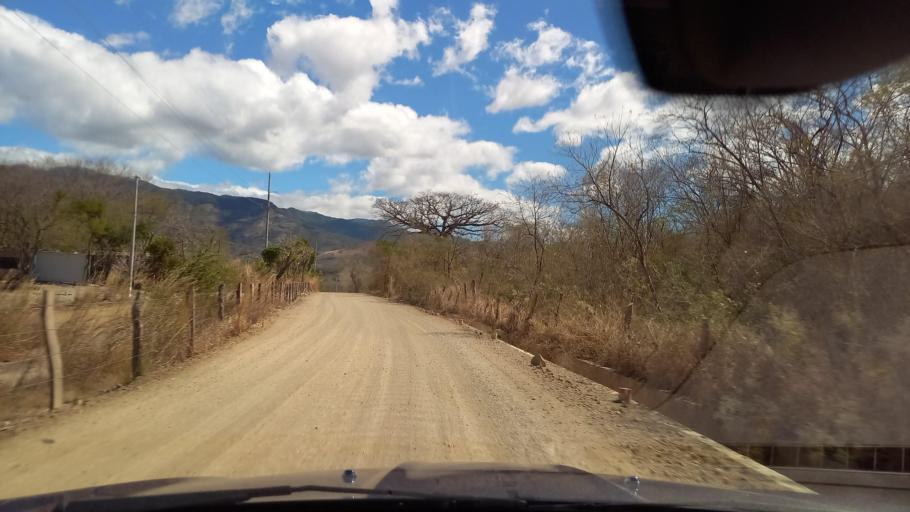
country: SV
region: Santa Ana
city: Metapan
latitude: 14.3601
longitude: -89.4727
